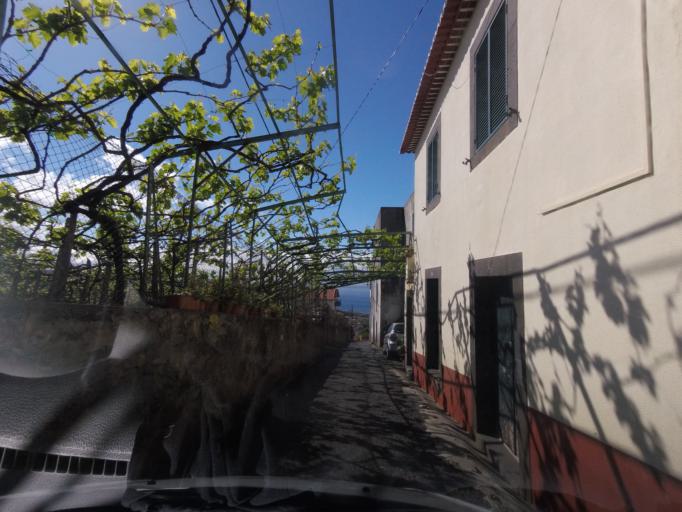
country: PT
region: Madeira
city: Camara de Lobos
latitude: 32.6636
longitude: -16.9750
